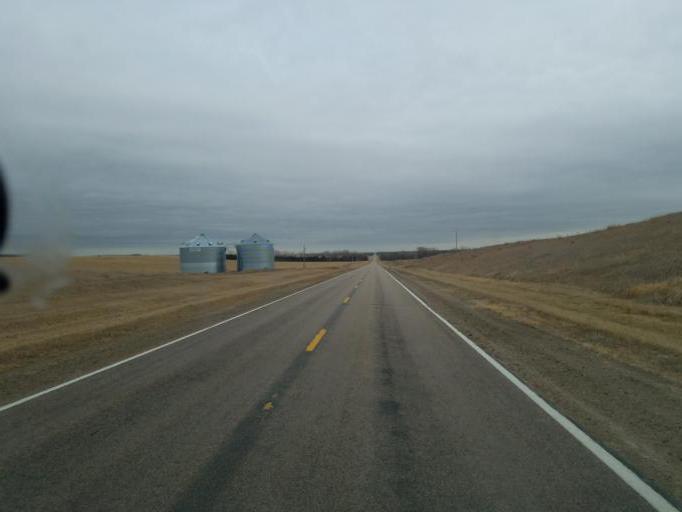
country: US
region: Nebraska
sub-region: Knox County
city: Bloomfield
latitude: 42.6127
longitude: -97.4780
